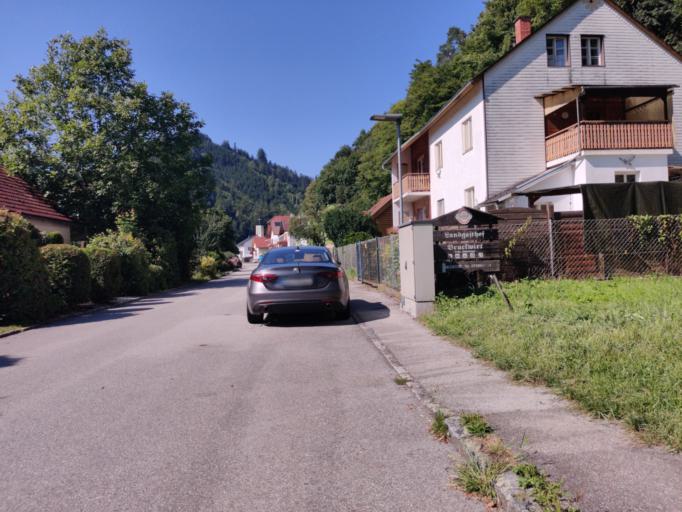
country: AT
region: Upper Austria
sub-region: Politischer Bezirk Rohrbach
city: Atzesberg
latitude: 48.4480
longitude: 13.9222
